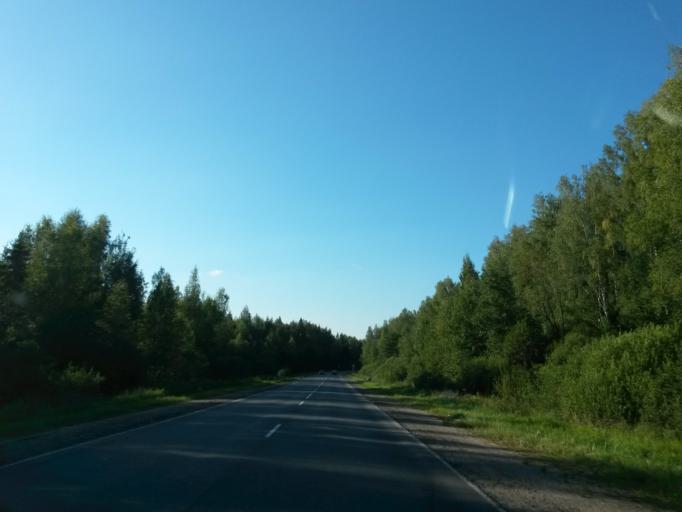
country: RU
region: Ivanovo
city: Pistsovo
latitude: 57.1011
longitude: 40.6549
